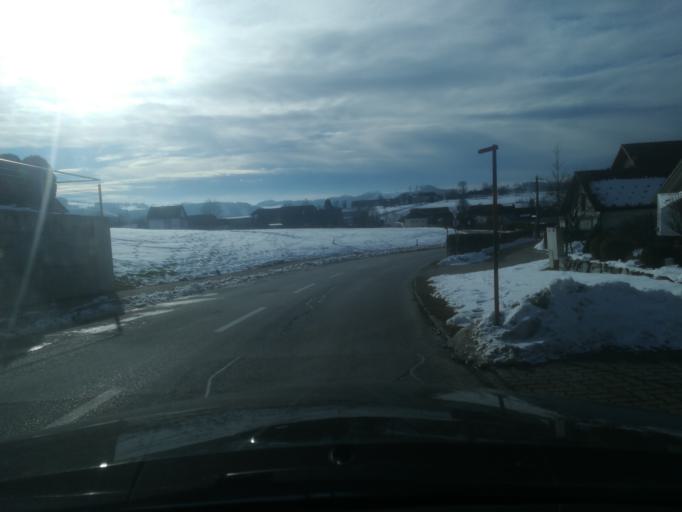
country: AT
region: Upper Austria
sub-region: Politischer Bezirk Perg
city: Perg
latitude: 48.3222
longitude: 14.6249
